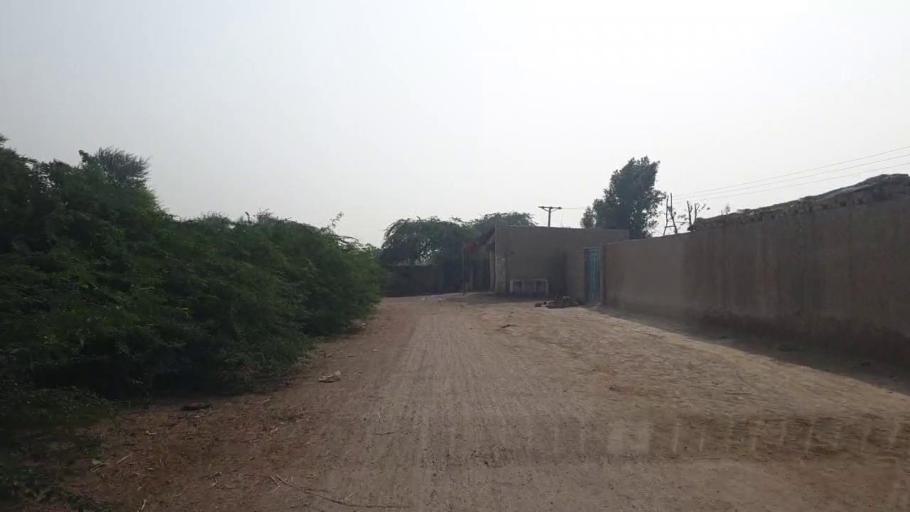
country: PK
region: Sindh
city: Tando Muhammad Khan
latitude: 25.2611
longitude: 68.5124
